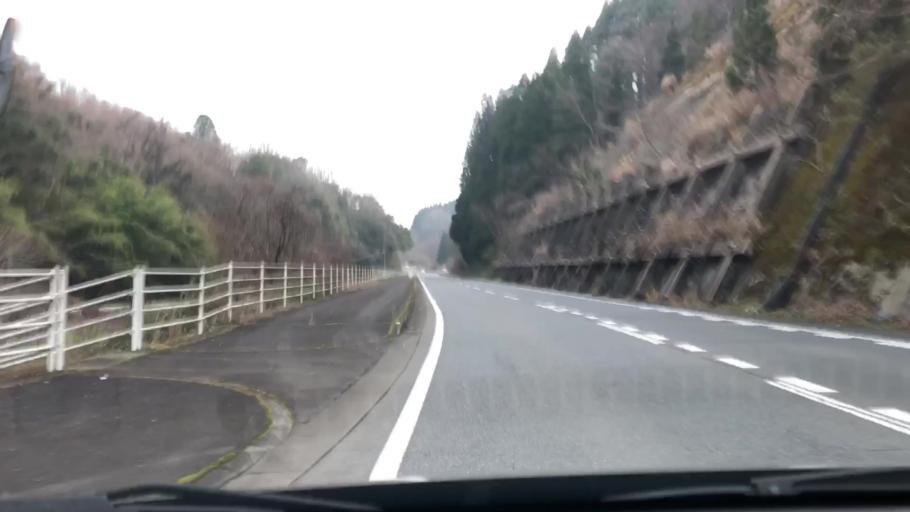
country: JP
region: Oita
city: Takedamachi
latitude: 32.9775
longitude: 131.5483
